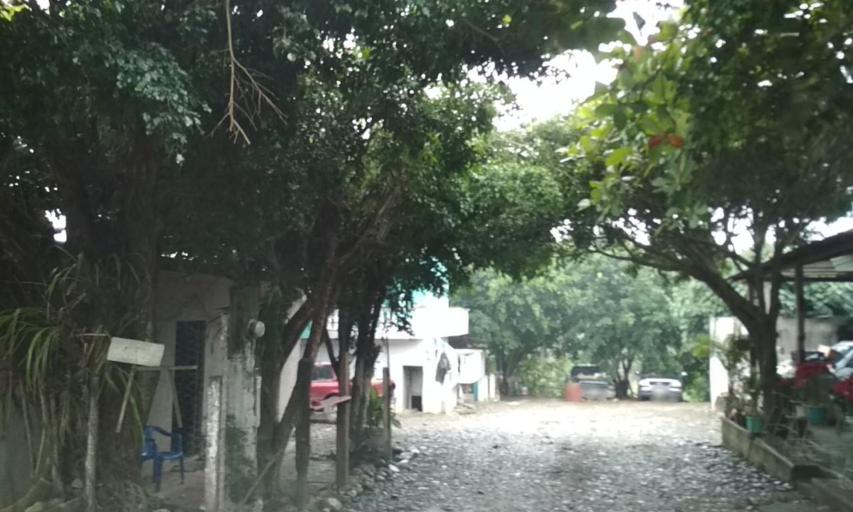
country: MX
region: Puebla
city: Espinal
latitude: 20.3286
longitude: -97.3935
